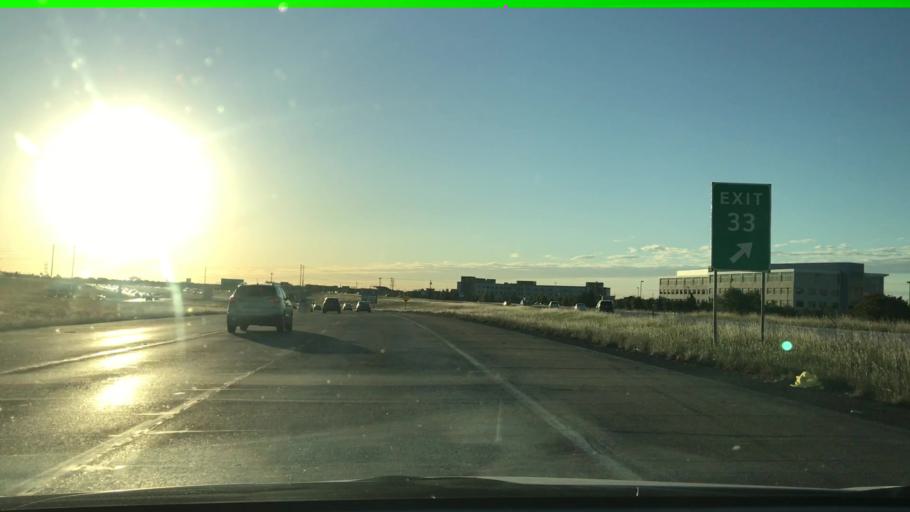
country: US
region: Texas
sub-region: Dallas County
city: Coppell
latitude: 32.9254
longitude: -96.9993
